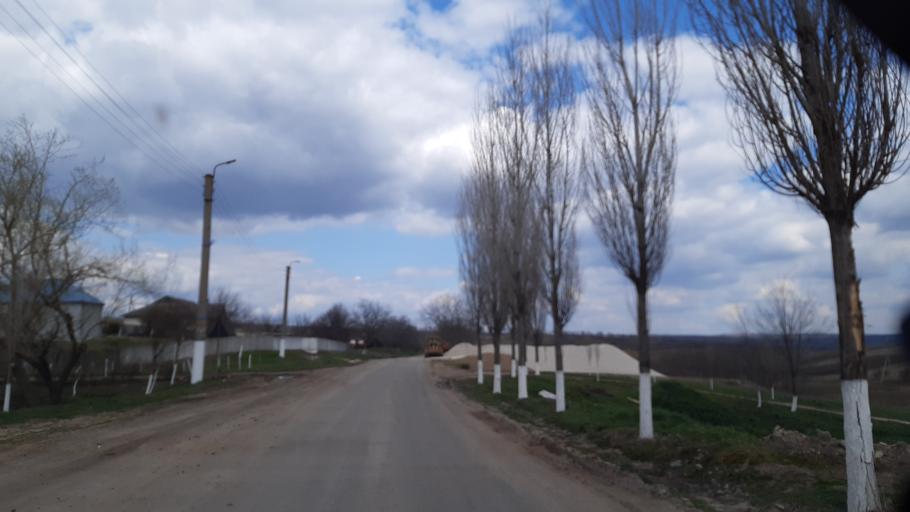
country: MD
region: Laloveni
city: Ialoveni
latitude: 46.8866
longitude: 28.6962
